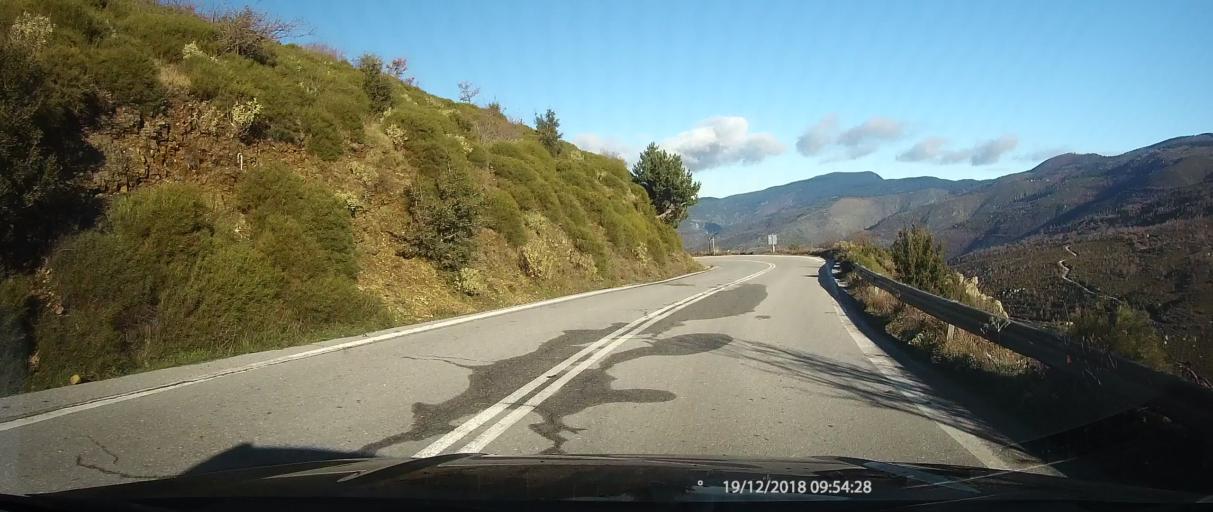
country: GR
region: Peloponnese
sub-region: Nomos Messinias
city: Paralia Vergas
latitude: 37.0805
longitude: 22.2468
